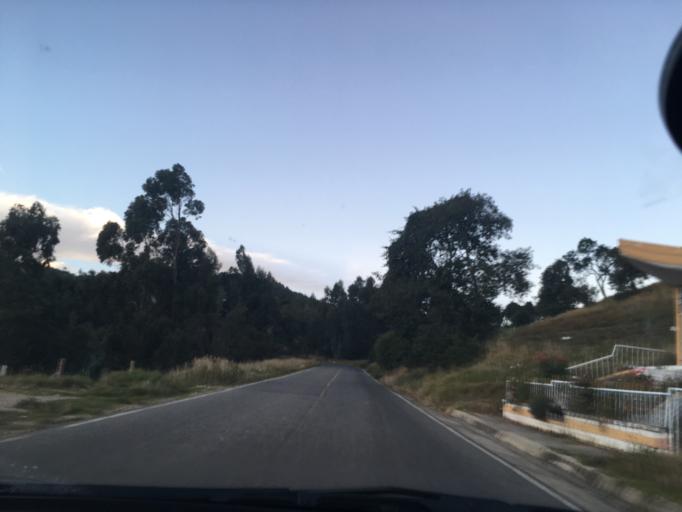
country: CO
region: Boyaca
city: Aquitania
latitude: 5.6016
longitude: -72.9101
